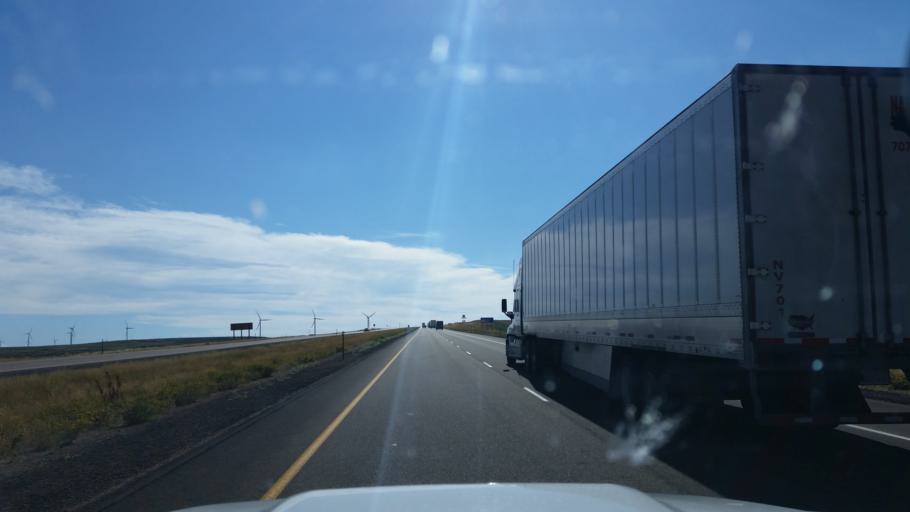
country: US
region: Wyoming
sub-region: Uinta County
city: Mountain View
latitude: 41.3188
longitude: -110.4903
